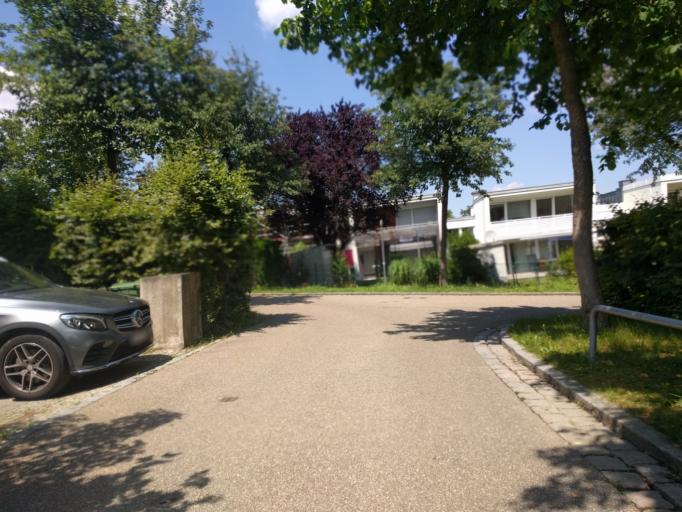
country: DE
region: Bavaria
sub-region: Upper Palatinate
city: Pentling
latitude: 48.9946
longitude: 12.0790
